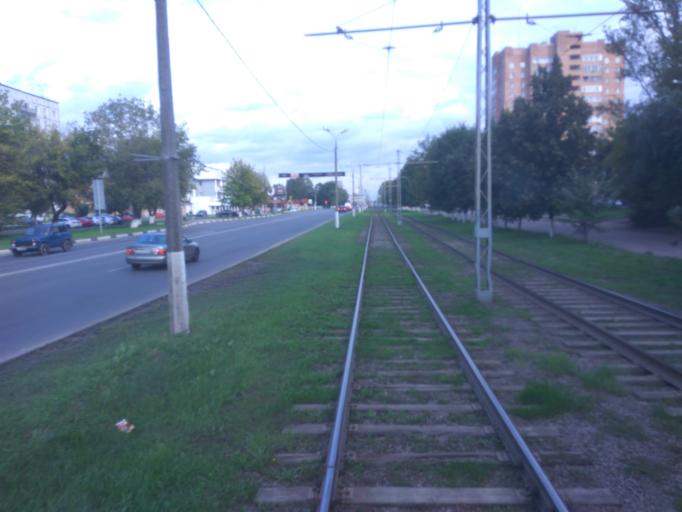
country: RU
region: Moskovskaya
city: Kolomna
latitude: 55.0870
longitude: 38.7925
